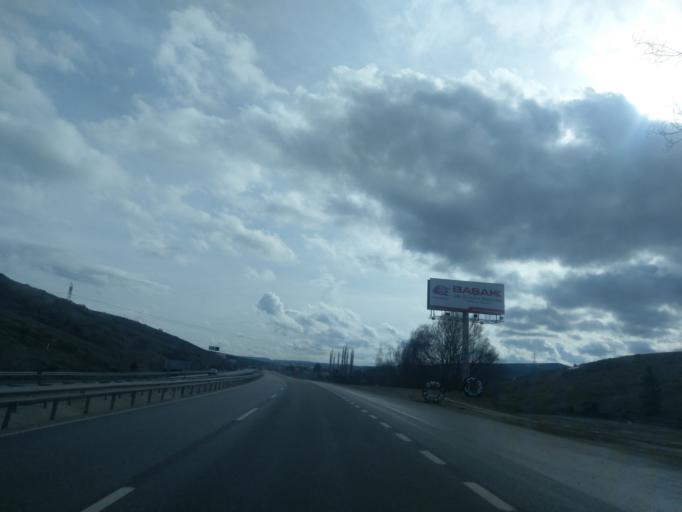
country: TR
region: Eskisehir
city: Inonu
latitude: 39.7022
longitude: 30.1541
